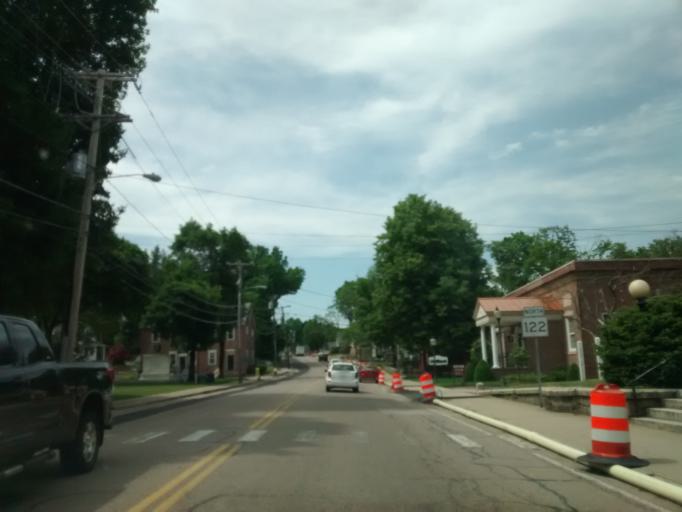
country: US
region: Massachusetts
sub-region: Worcester County
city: Uxbridge
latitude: 42.0775
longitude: -71.6303
